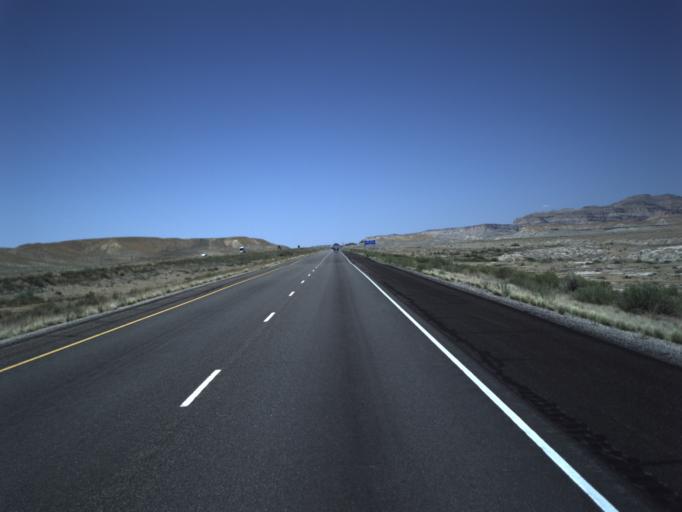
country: US
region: Utah
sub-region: Grand County
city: Moab
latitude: 38.9467
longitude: -109.6565
